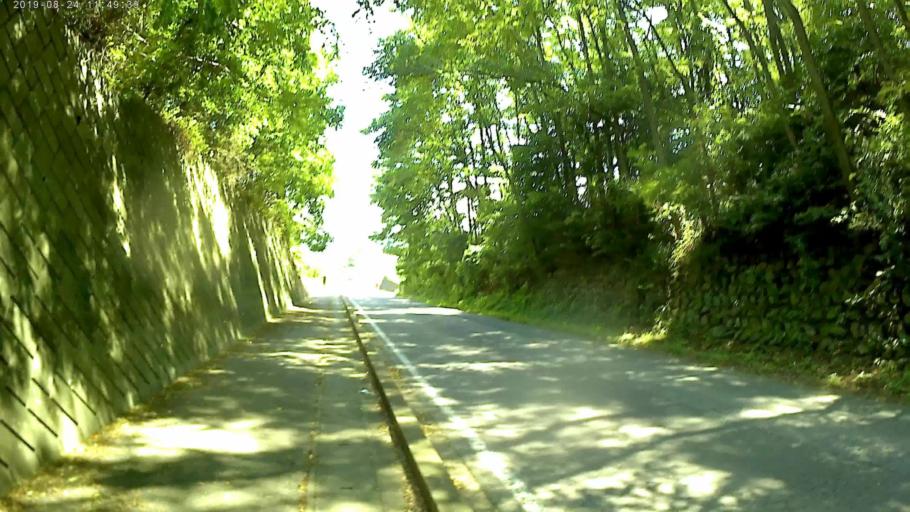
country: JP
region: Nagano
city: Kamimaruko
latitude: 36.2717
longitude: 138.3473
